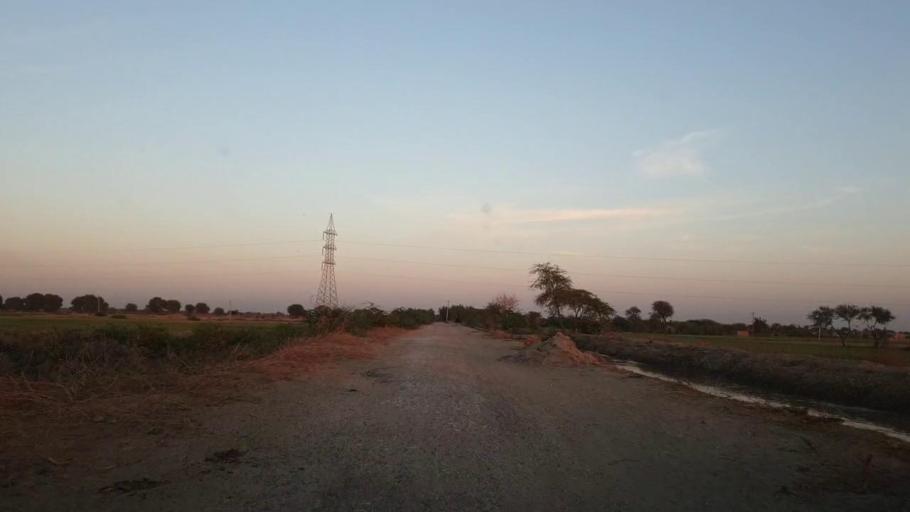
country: PK
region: Sindh
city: Kunri
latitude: 25.1469
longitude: 69.4419
